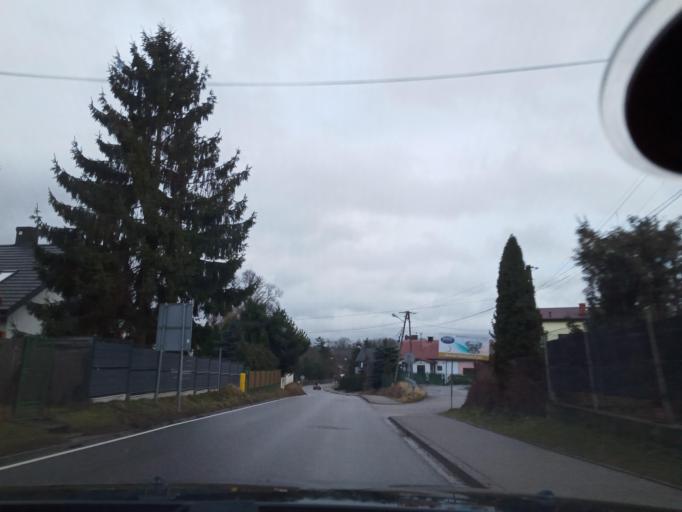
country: PL
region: Lesser Poland Voivodeship
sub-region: Powiat wielicki
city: Kokotow
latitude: 50.0090
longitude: 20.0846
